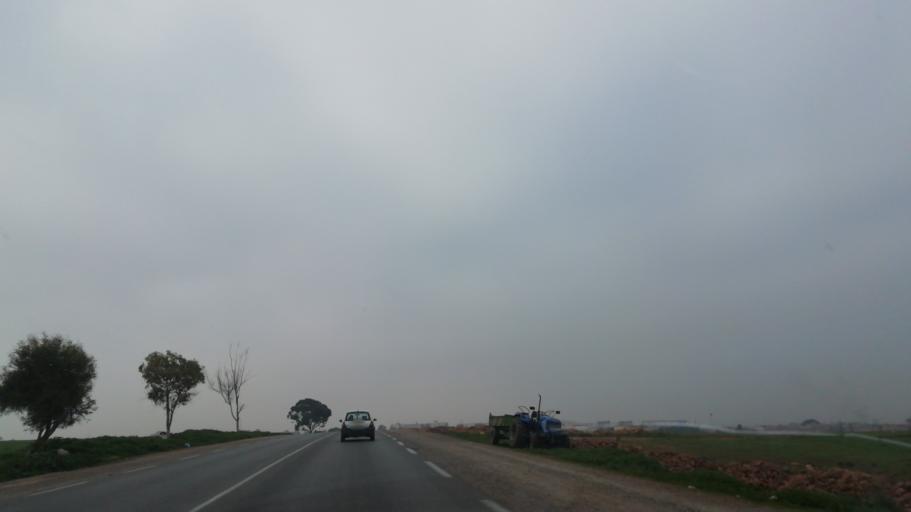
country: DZ
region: Relizane
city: Djidiouia
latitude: 35.8956
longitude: 0.7473
